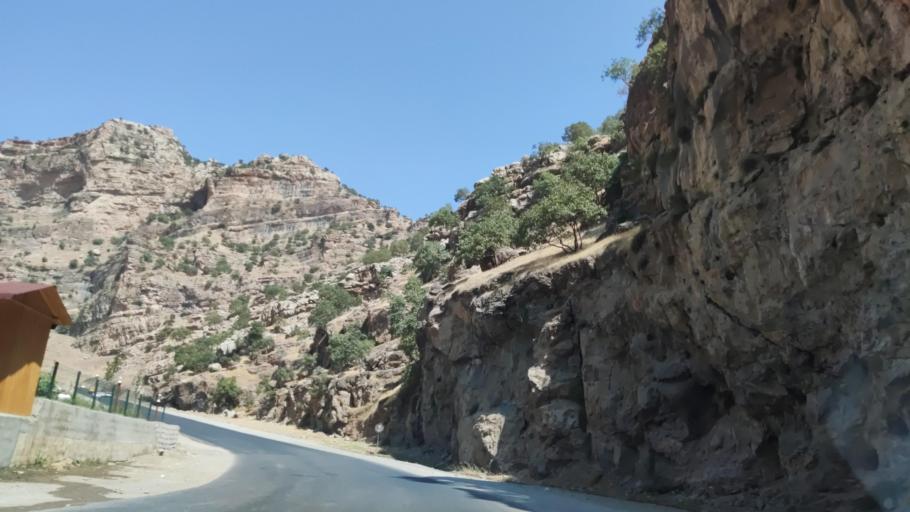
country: IQ
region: Arbil
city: Ruwandiz
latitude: 36.6300
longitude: 44.4490
